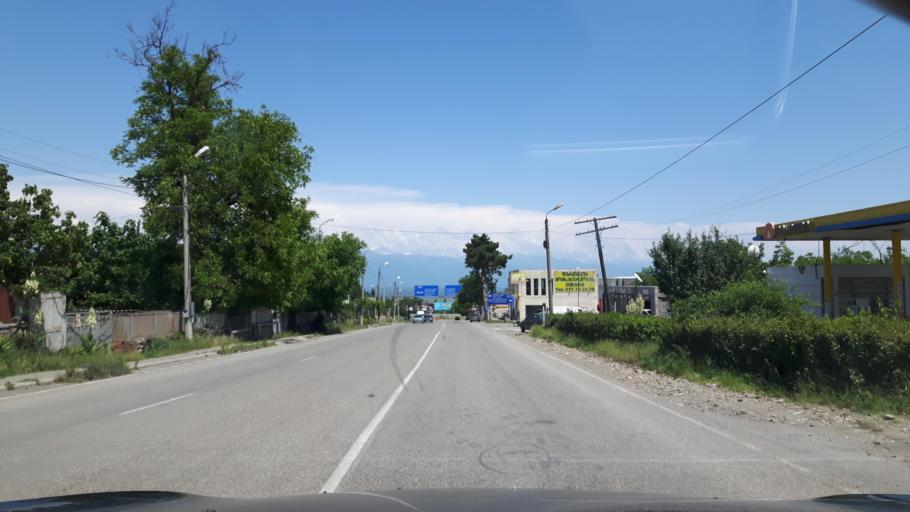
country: GE
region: Kakheti
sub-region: Gurjaani
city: Gurjaani
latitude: 41.6901
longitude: 45.8561
